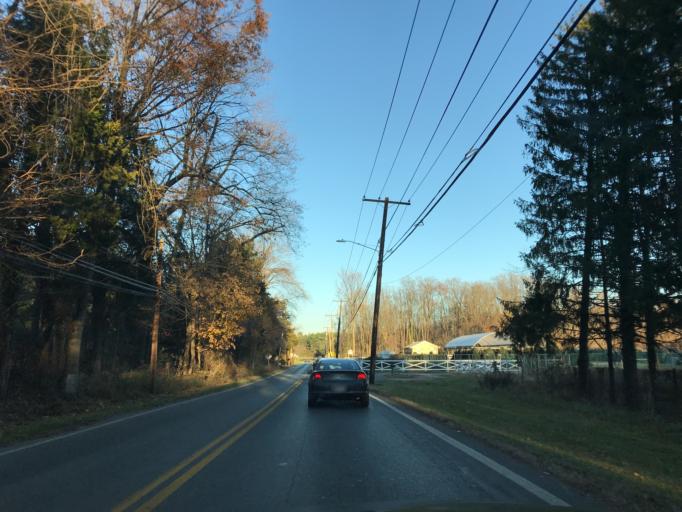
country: US
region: Maryland
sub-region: Montgomery County
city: Olney
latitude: 39.1469
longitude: -77.0376
